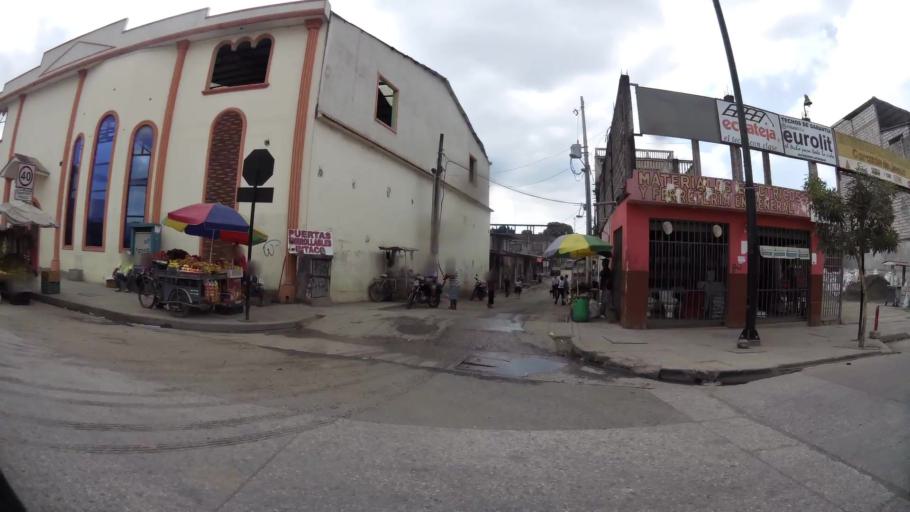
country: EC
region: Guayas
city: Santa Lucia
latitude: -2.1045
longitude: -79.9533
